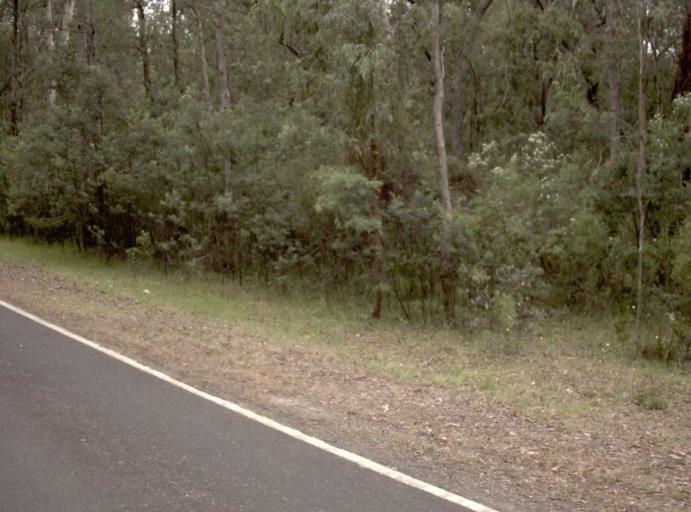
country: AU
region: Victoria
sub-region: East Gippsland
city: Bairnsdale
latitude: -37.6330
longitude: 147.2233
